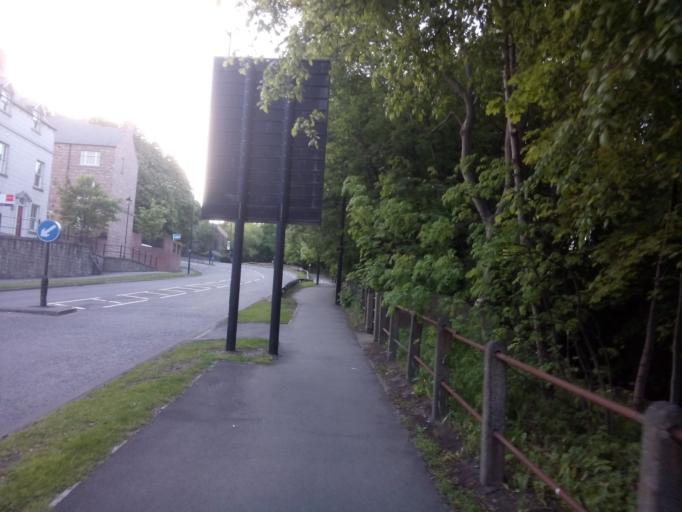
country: GB
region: England
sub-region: County Durham
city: Durham
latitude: 54.7795
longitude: -1.5794
